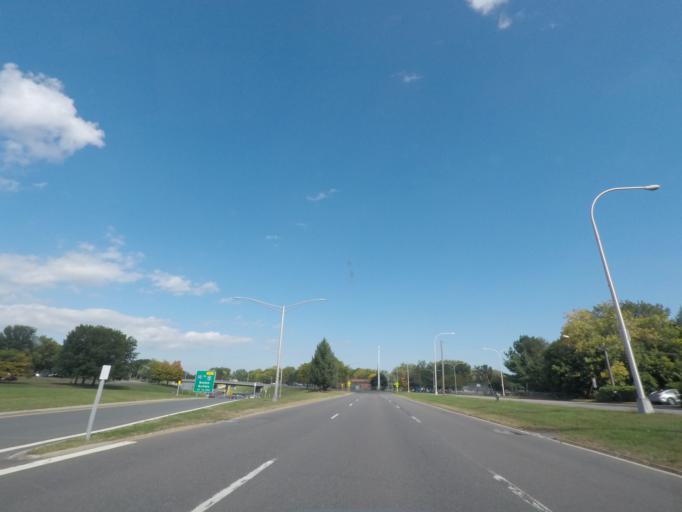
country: US
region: New York
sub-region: Albany County
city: Roessleville
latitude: 42.6752
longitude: -73.8031
